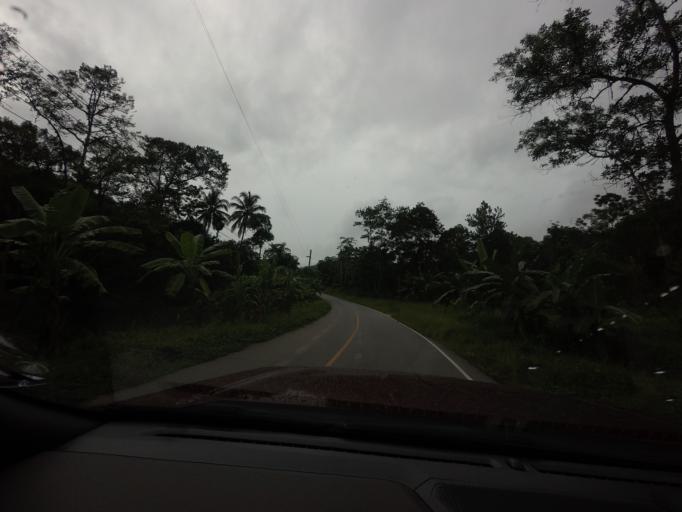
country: TH
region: Narathiwat
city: Chanae
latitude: 6.0284
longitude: 101.6955
